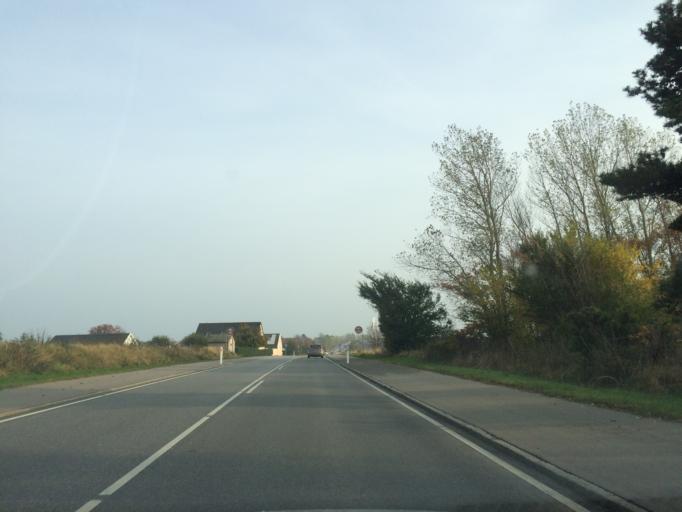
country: DK
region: Zealand
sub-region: Odsherred Kommune
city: Asnaes
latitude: 55.9773
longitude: 11.3307
